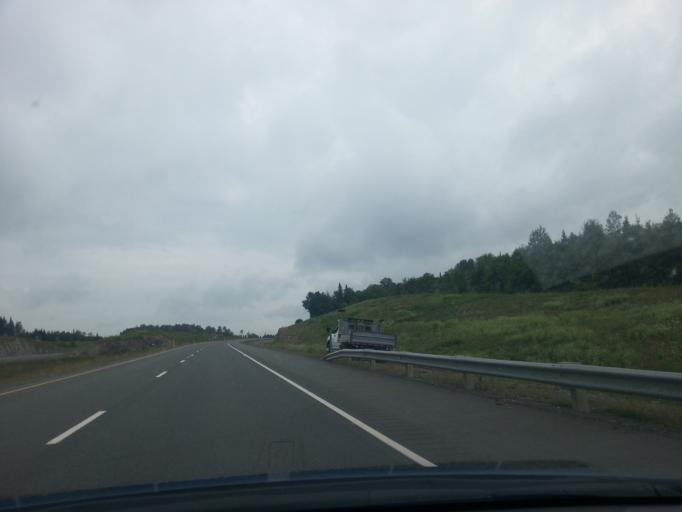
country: US
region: Maine
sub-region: Aroostook County
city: Easton
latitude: 46.5912
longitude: -67.7425
